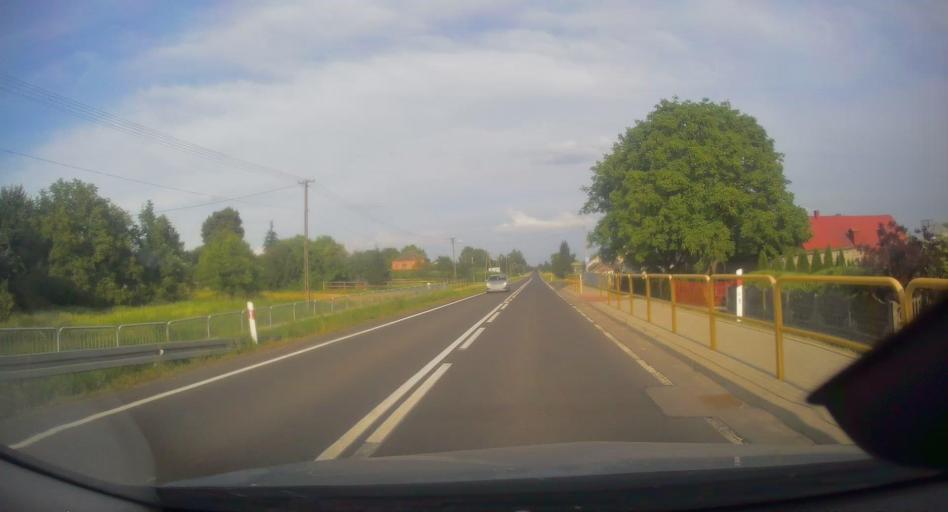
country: PL
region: Lesser Poland Voivodeship
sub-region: Powiat bochenski
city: Dziewin
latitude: 50.1447
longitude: 20.4478
